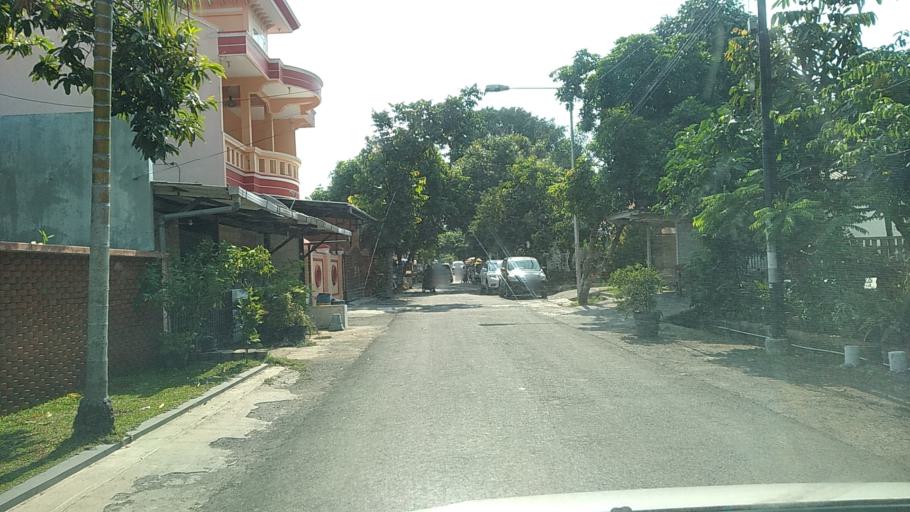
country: ID
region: Central Java
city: Ungaran
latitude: -7.0681
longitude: 110.4225
